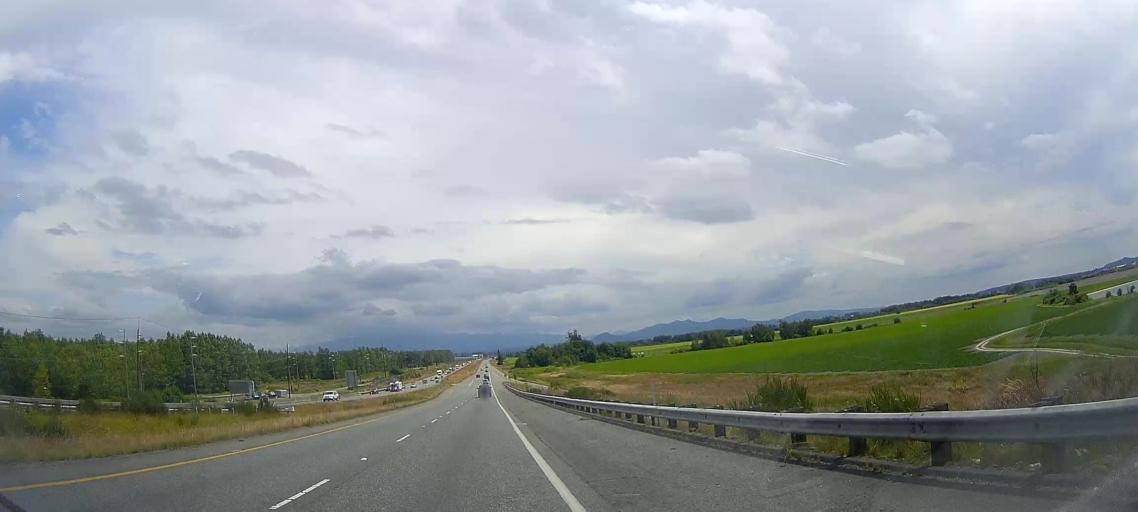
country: US
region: Washington
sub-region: Skagit County
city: Anacortes
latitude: 48.4531
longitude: -122.5079
